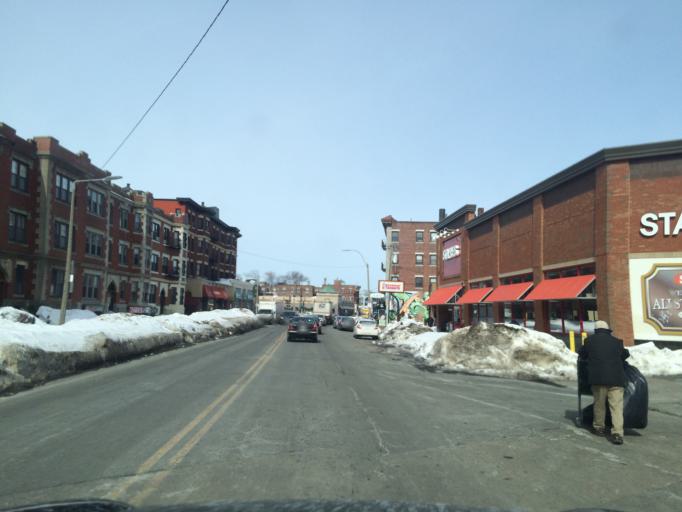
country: US
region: Massachusetts
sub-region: Norfolk County
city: Brookline
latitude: 42.3493
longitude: -71.1301
